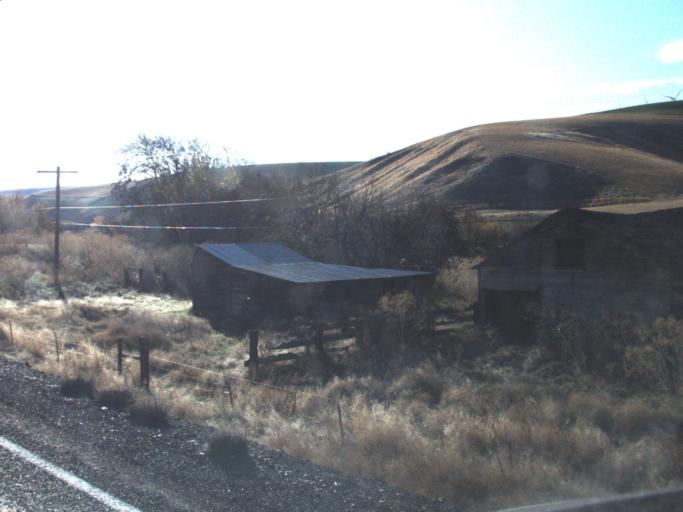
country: US
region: Washington
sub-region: Garfield County
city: Pomeroy
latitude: 46.5192
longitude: -117.7977
